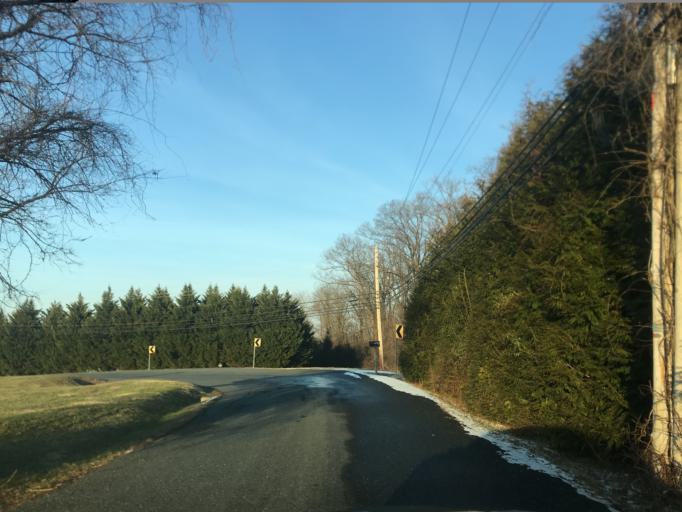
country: US
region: Maryland
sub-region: Harford County
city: Edgewood
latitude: 39.4381
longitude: -76.2662
